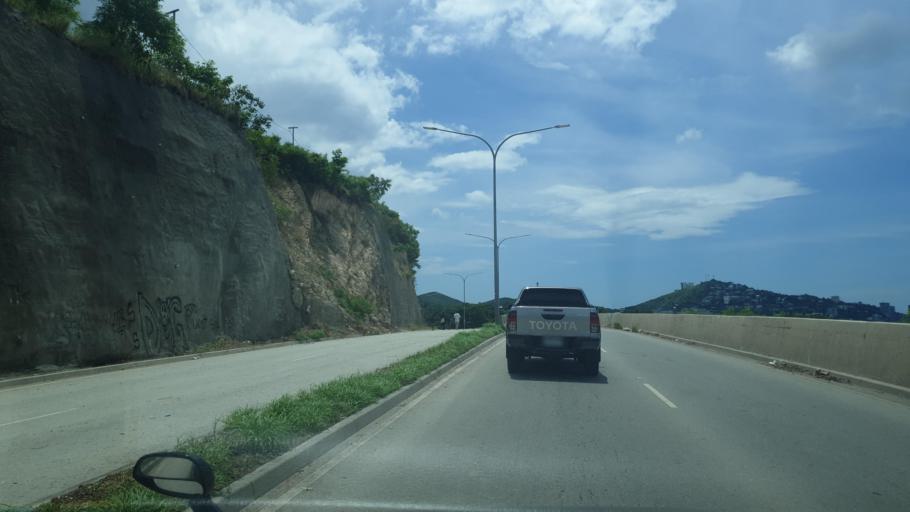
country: PG
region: National Capital
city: Port Moresby
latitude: -9.4482
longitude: 147.1479
